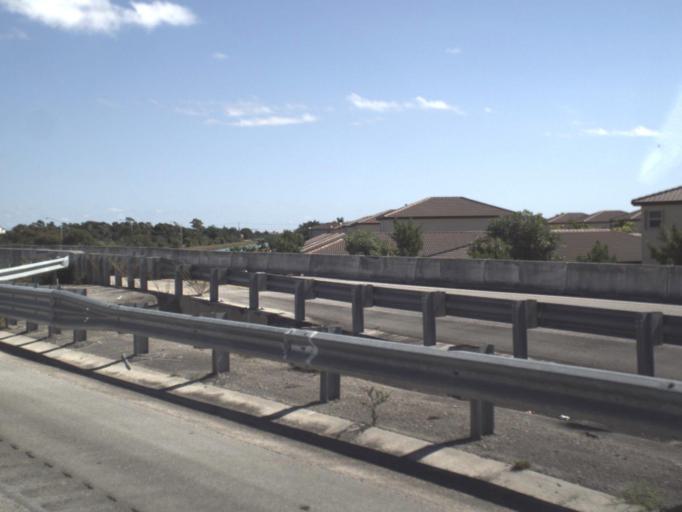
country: US
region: Florida
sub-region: Miami-Dade County
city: Leisure City
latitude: 25.4742
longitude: -80.4447
